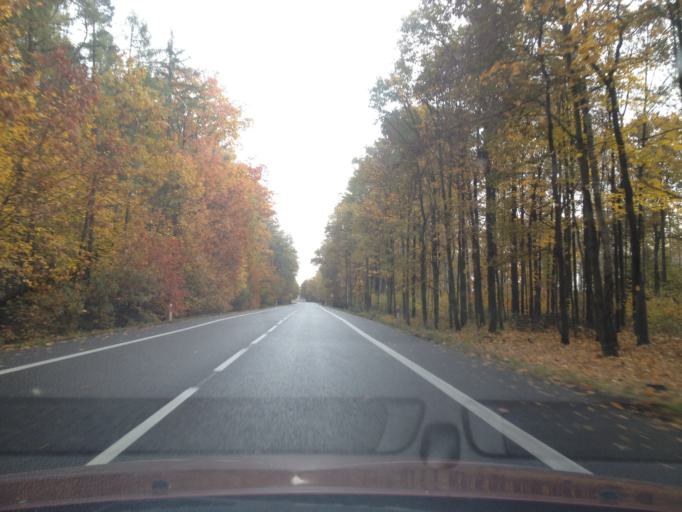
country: PL
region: Lower Silesian Voivodeship
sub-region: Powiat zgorzelecki
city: Lagow
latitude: 51.1534
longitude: 15.0756
